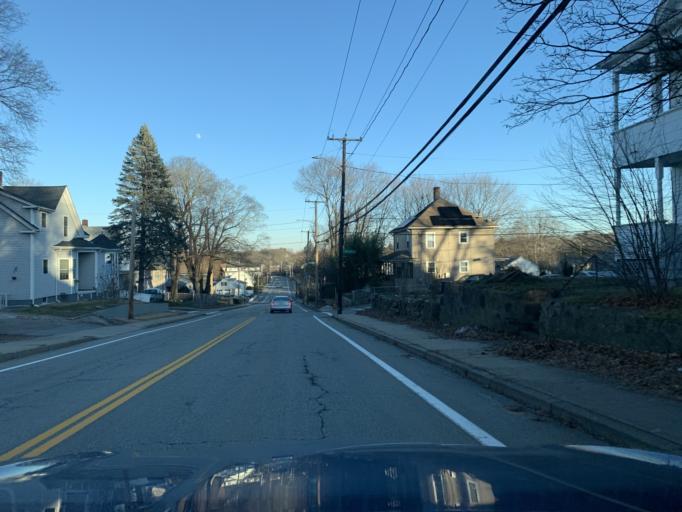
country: US
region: Rhode Island
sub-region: Kent County
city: West Warwick
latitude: 41.6957
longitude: -71.5299
